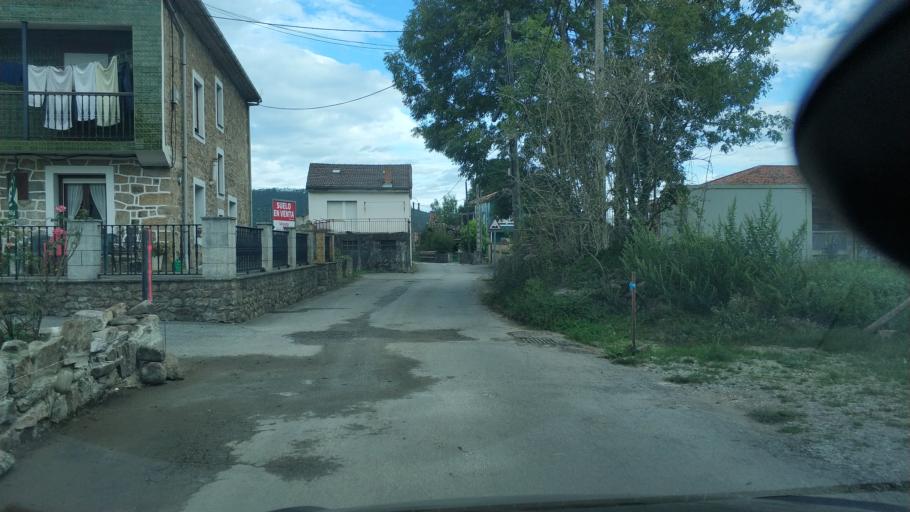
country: ES
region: Cantabria
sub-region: Provincia de Cantabria
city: Santa Maria de Cayon
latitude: 43.3031
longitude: -3.8563
